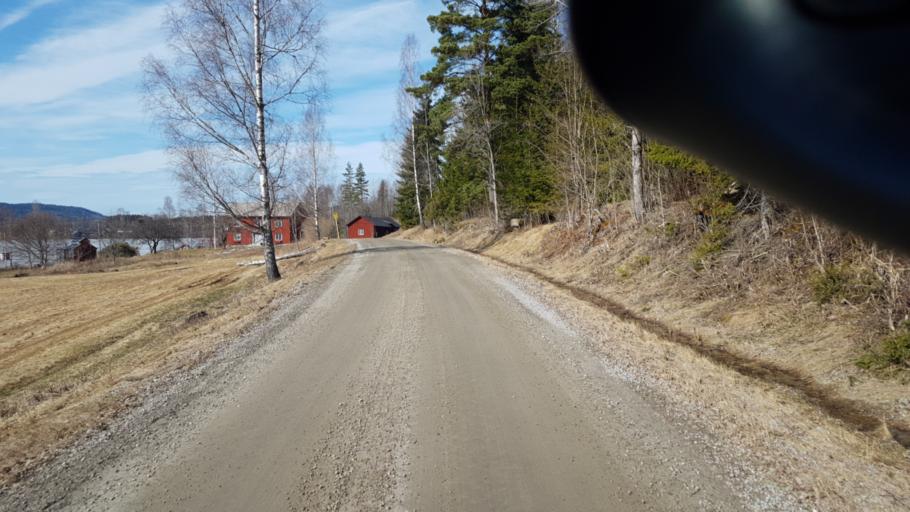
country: SE
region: Vaermland
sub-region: Arvika Kommun
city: Arvika
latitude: 59.7328
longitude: 12.8332
